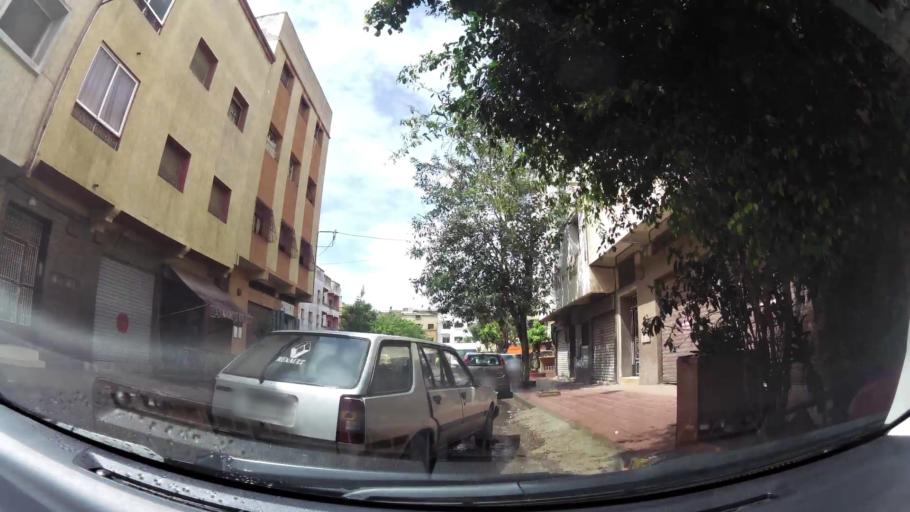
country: MA
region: Grand Casablanca
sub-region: Casablanca
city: Casablanca
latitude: 33.5520
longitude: -7.6760
